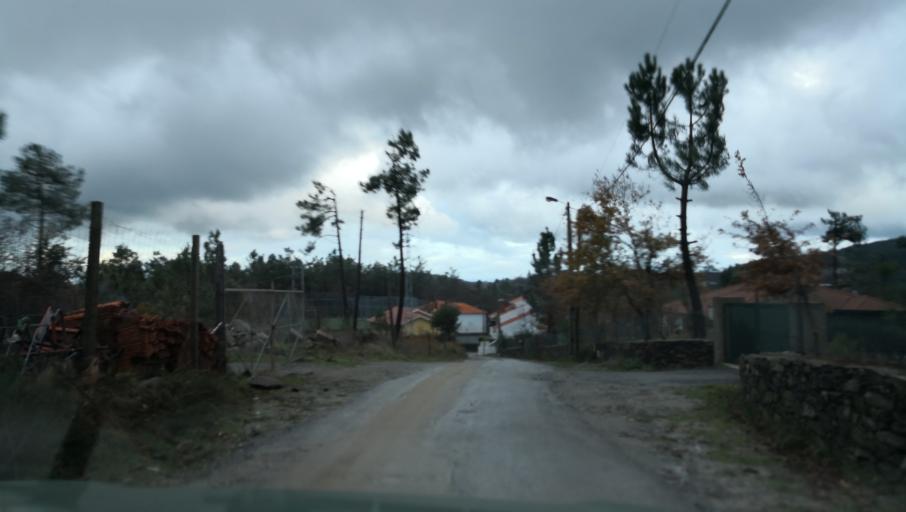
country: PT
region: Vila Real
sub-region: Santa Marta de Penaguiao
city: Santa Marta de Penaguiao
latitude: 41.2938
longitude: -7.8811
